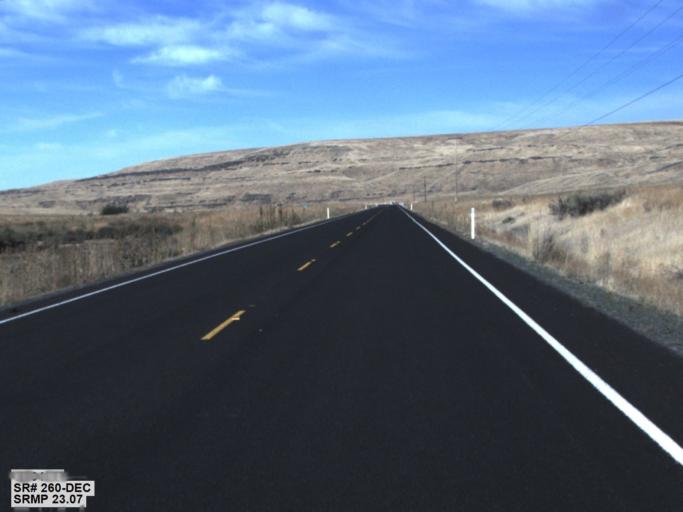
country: US
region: Washington
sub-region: Franklin County
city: Connell
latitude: 46.6484
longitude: -118.5913
